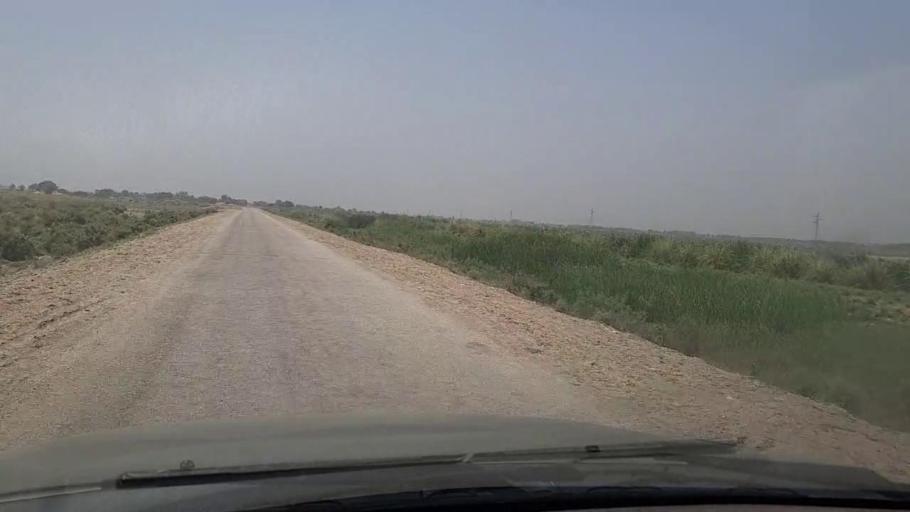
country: PK
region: Sindh
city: Ratodero
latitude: 27.7913
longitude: 68.2268
